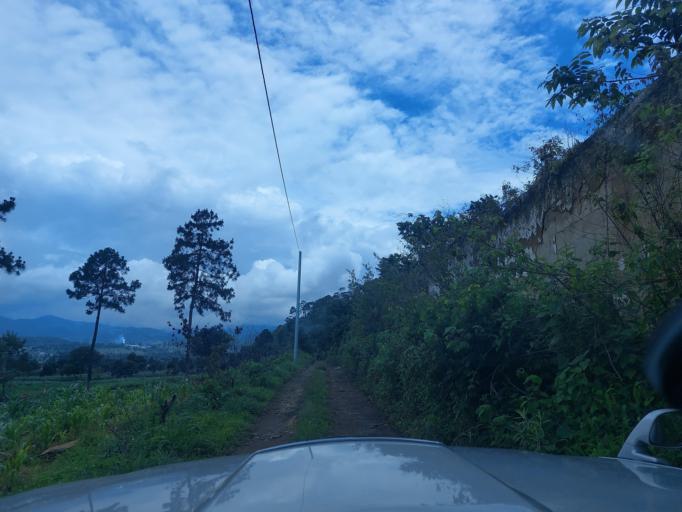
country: GT
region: Chimaltenango
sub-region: Municipio de Chimaltenango
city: Chimaltenango
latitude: 14.6470
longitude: -90.8292
